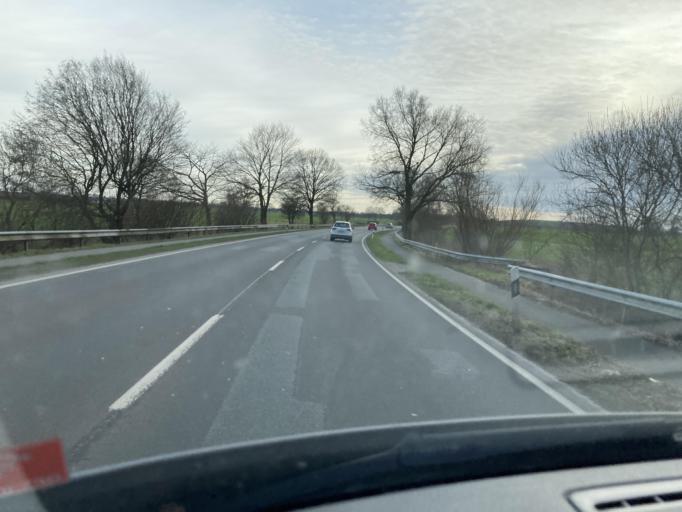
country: DE
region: Lower Saxony
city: Leer
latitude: 53.2171
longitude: 7.4848
